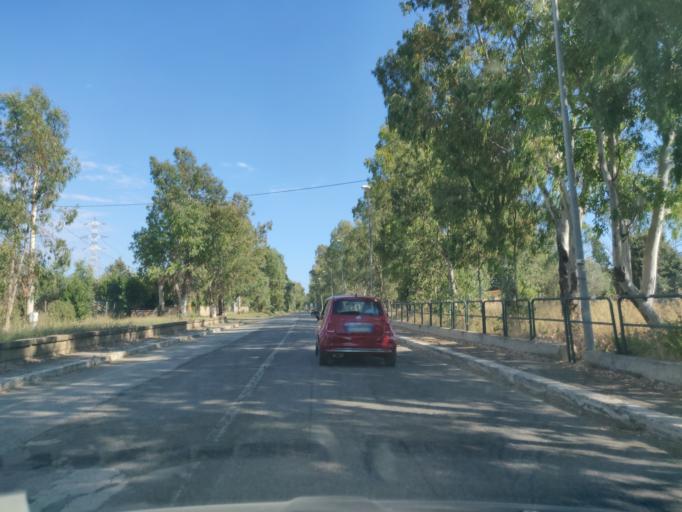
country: IT
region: Latium
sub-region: Citta metropolitana di Roma Capitale
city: Aurelia
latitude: 42.1513
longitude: 11.7585
